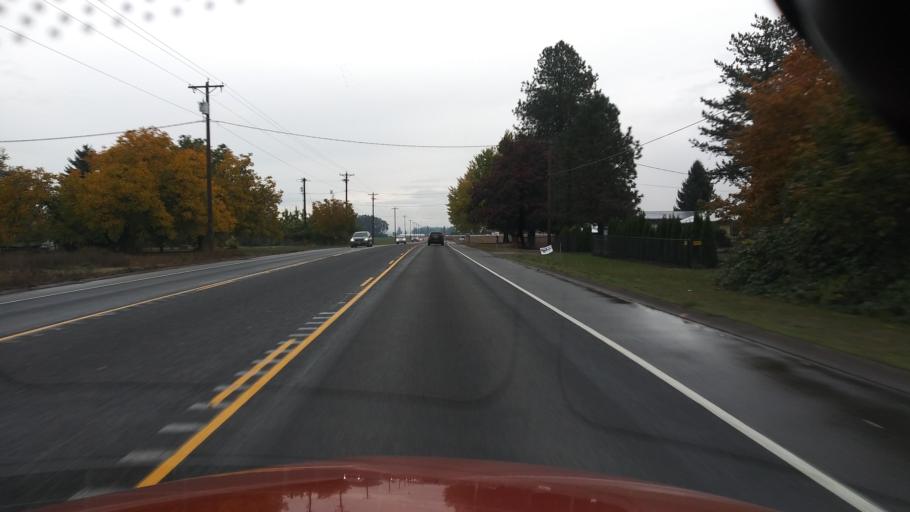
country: US
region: Oregon
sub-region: Washington County
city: Cornelius
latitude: 45.5573
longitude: -123.0596
